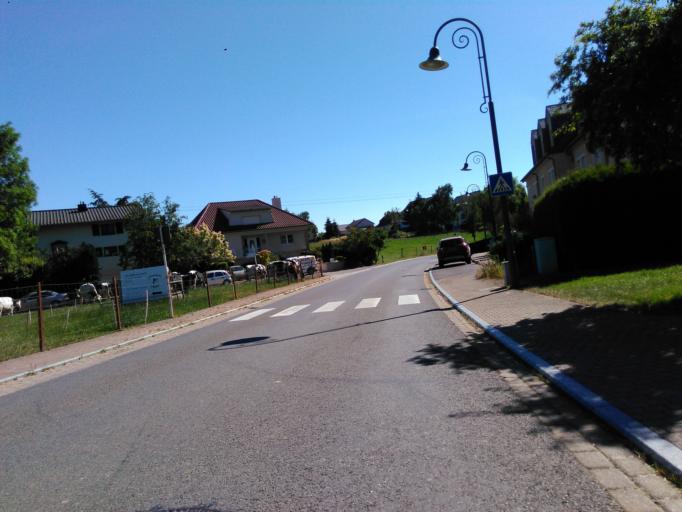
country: LU
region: Luxembourg
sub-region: Canton d'Esch-sur-Alzette
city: Mondercange
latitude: 49.5584
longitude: 5.9813
